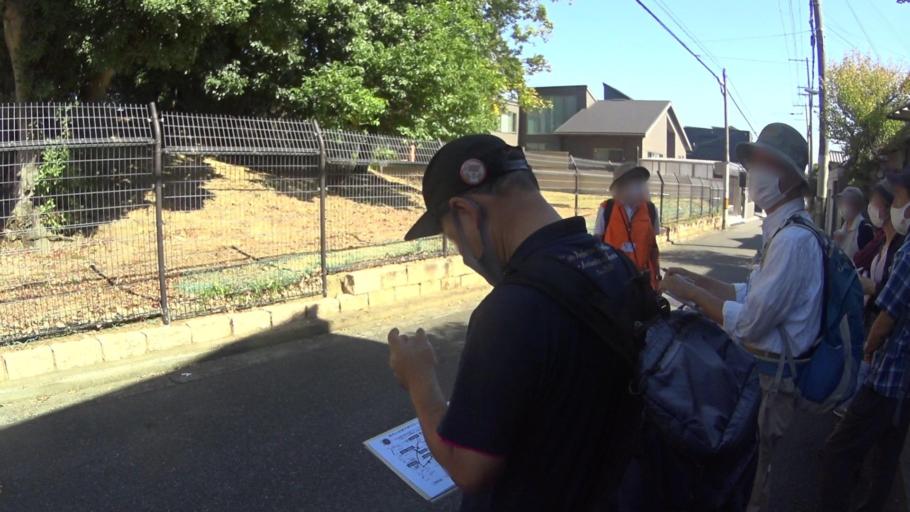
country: JP
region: Ehime
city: Kihoku-cho
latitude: 33.4128
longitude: 132.8958
